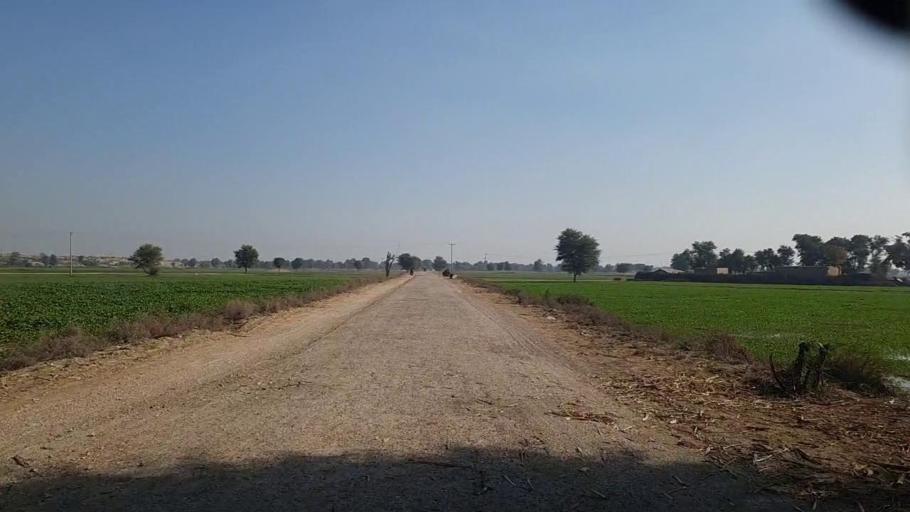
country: PK
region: Sindh
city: Darya Khan Marri
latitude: 26.6682
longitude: 68.3332
